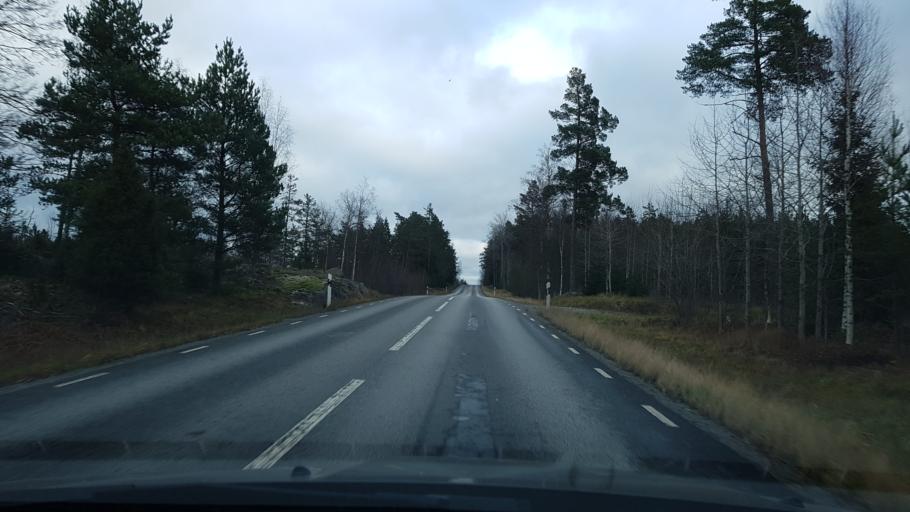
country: SE
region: Stockholm
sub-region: Norrtalje Kommun
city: Hallstavik
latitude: 60.0380
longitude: 18.5191
